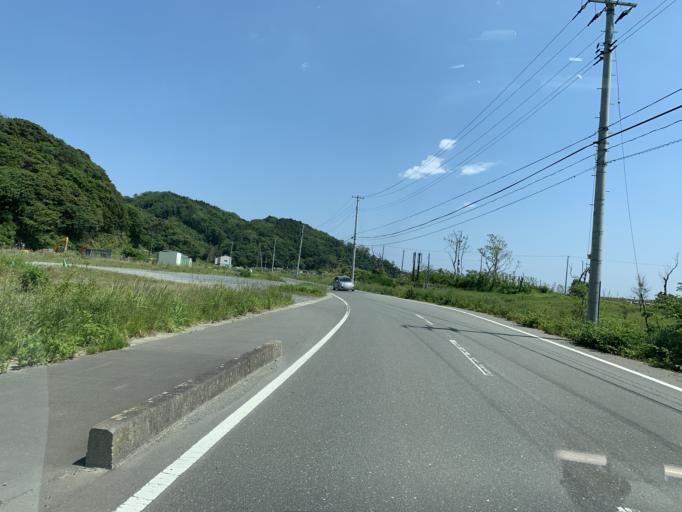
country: JP
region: Miyagi
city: Matsushima
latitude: 38.3298
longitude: 141.1626
